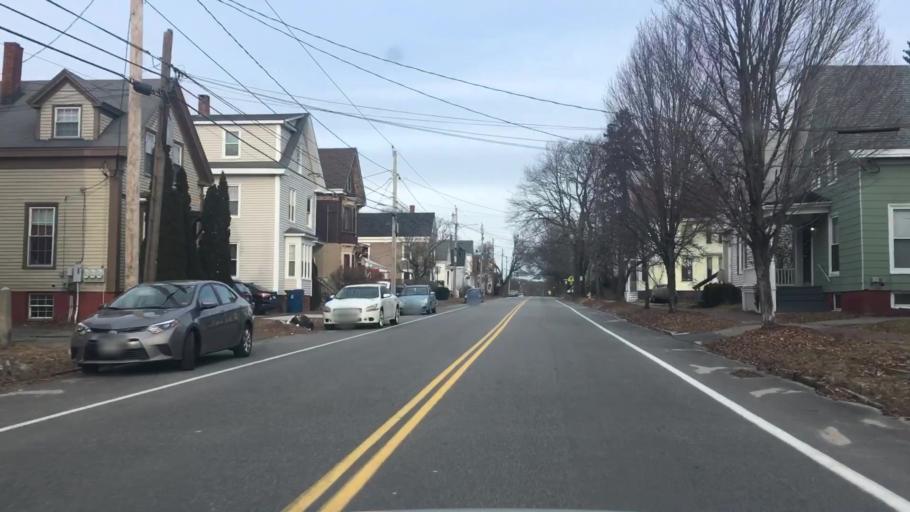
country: US
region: Maine
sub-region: Cumberland County
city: Portland
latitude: 43.6582
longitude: -70.2819
